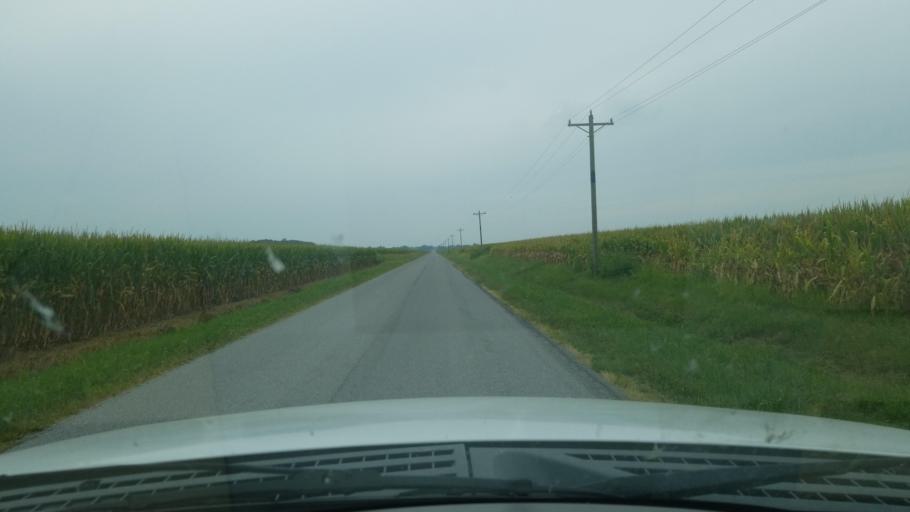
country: US
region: Illinois
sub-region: Saline County
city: Eldorado
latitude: 37.8670
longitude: -88.4560
